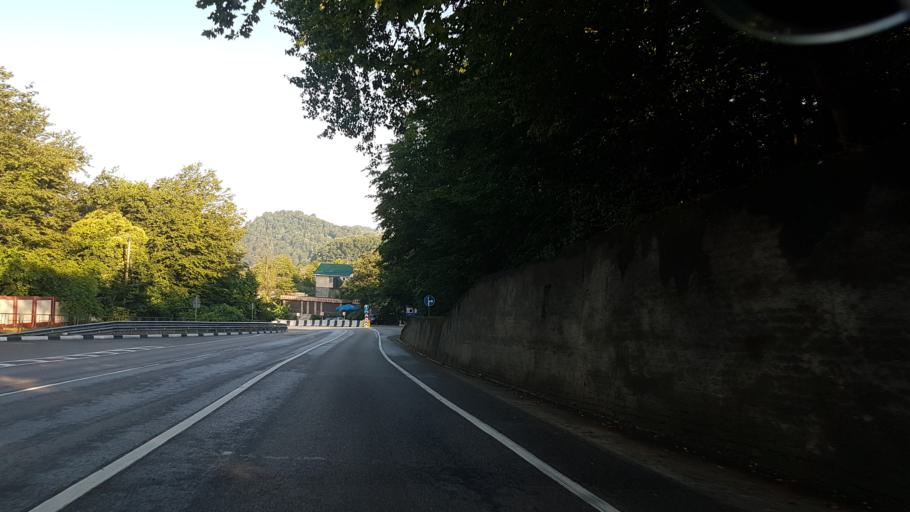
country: RU
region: Krasnodarskiy
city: Dagomys
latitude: 43.6622
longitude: 39.6797
